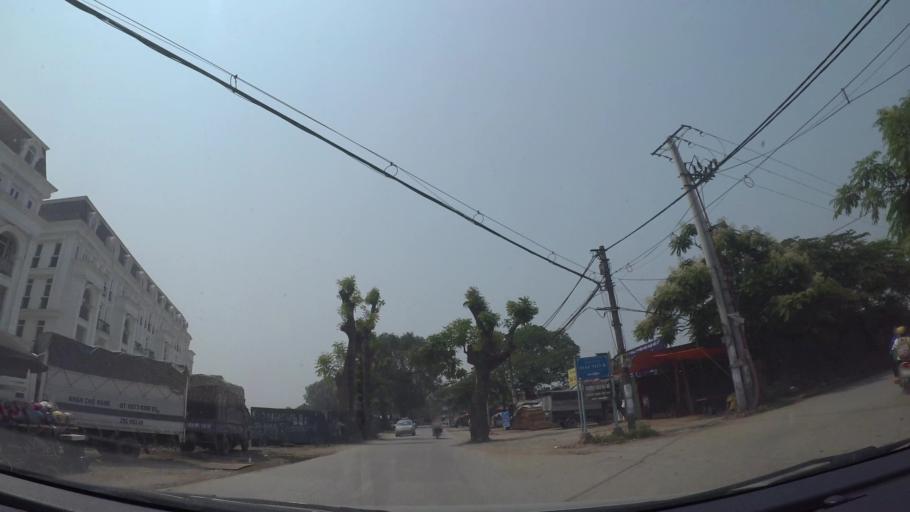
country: VN
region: Ha Noi
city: Ha Dong
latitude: 20.9881
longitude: 105.7663
